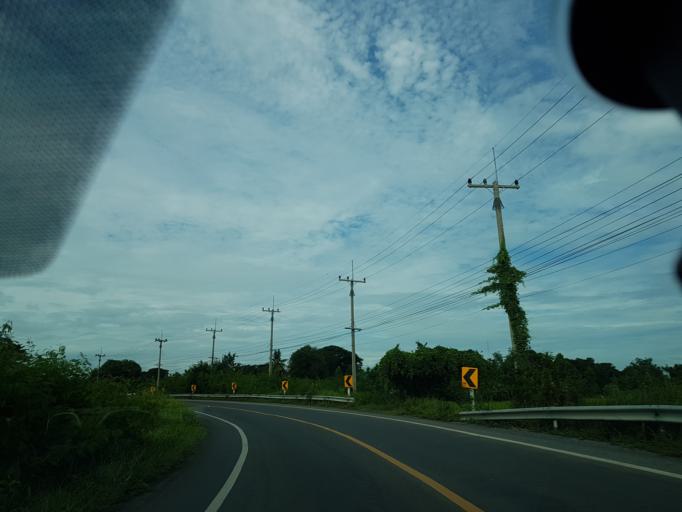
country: TH
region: Lop Buri
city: Tha Wung
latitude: 14.7446
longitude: 100.5431
